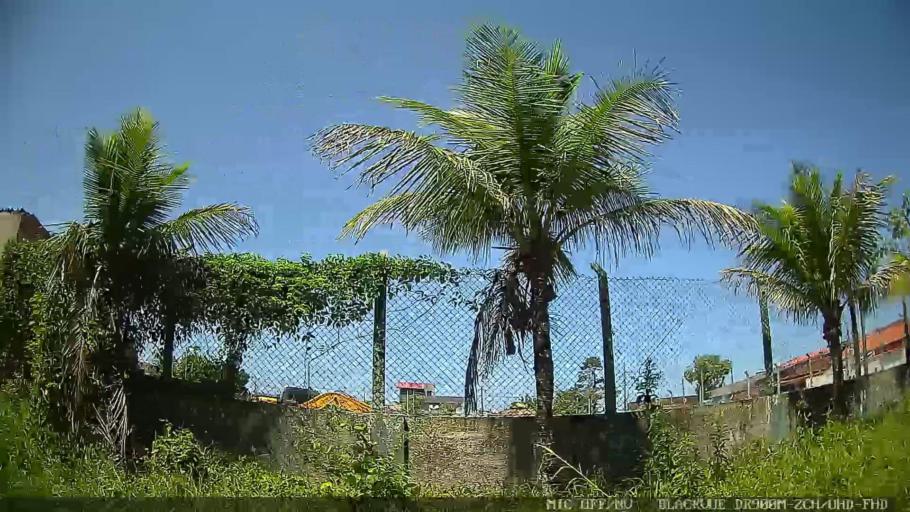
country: BR
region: Sao Paulo
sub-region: Peruibe
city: Peruibe
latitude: -24.2983
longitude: -46.9977
